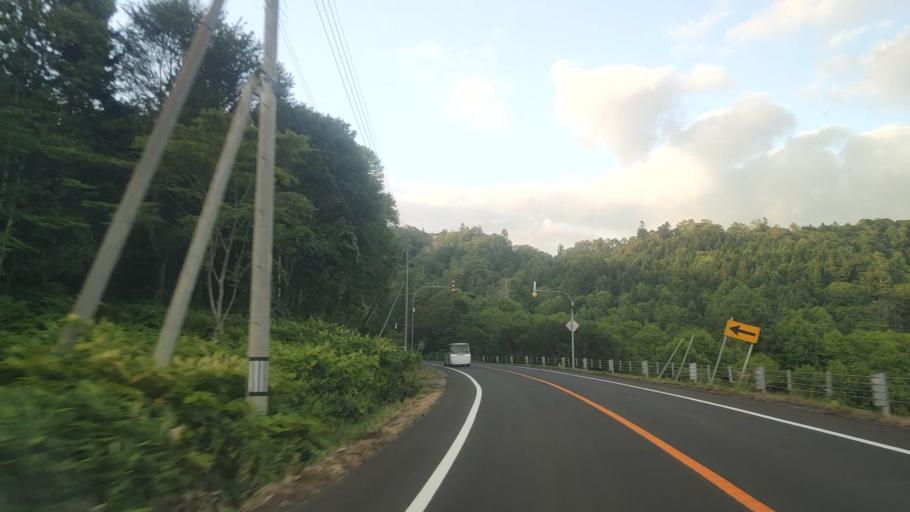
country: JP
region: Hokkaido
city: Bibai
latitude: 43.2854
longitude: 142.0694
